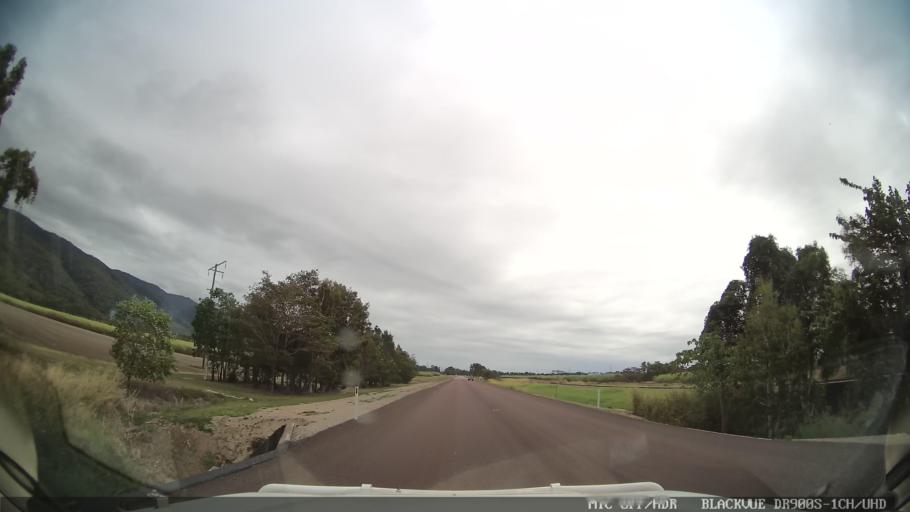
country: AU
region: Queensland
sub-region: Hinchinbrook
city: Ingham
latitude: -18.9236
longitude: 146.2610
